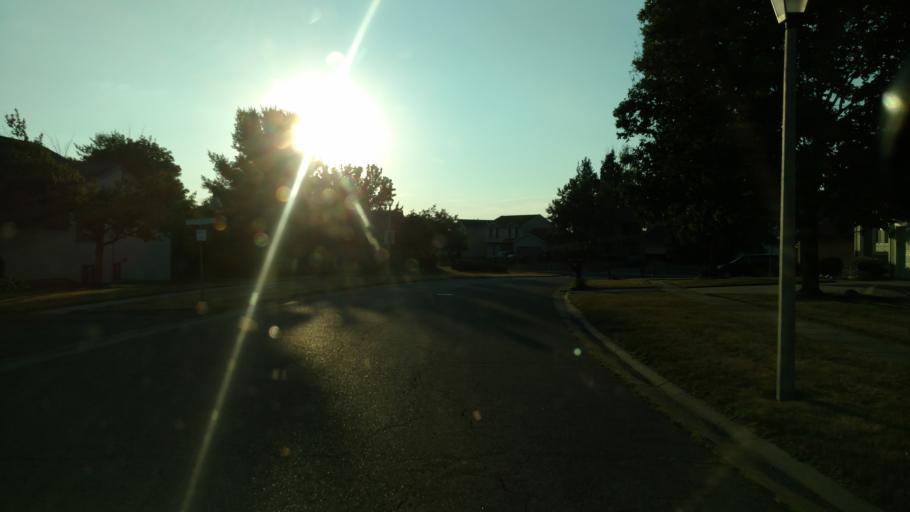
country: US
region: Michigan
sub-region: Eaton County
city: Waverly
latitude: 42.7212
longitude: -84.6189
